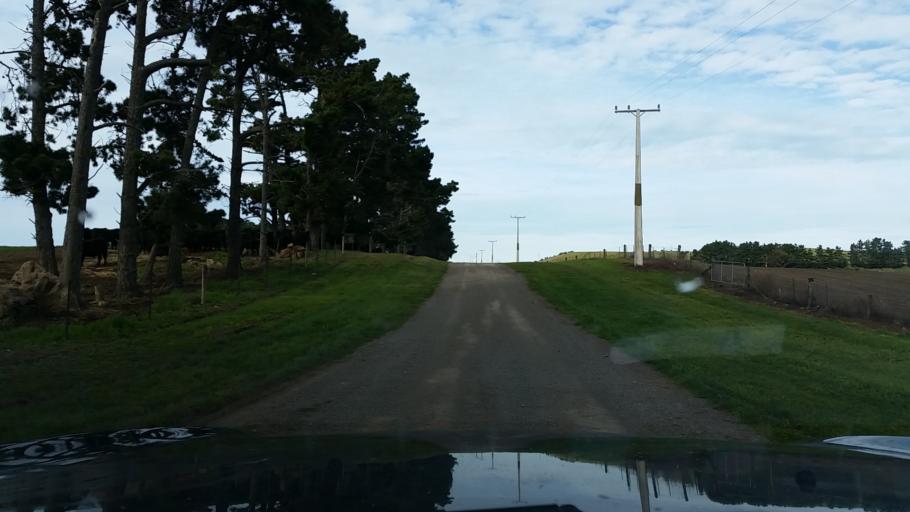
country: NZ
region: Marlborough
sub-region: Marlborough District
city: Blenheim
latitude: -41.6282
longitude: 174.1524
